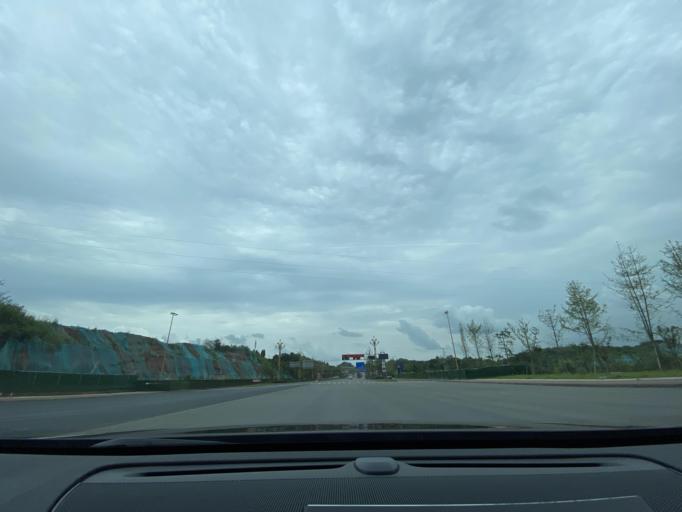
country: CN
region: Sichuan
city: Jiancheng
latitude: 30.4812
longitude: 104.4846
